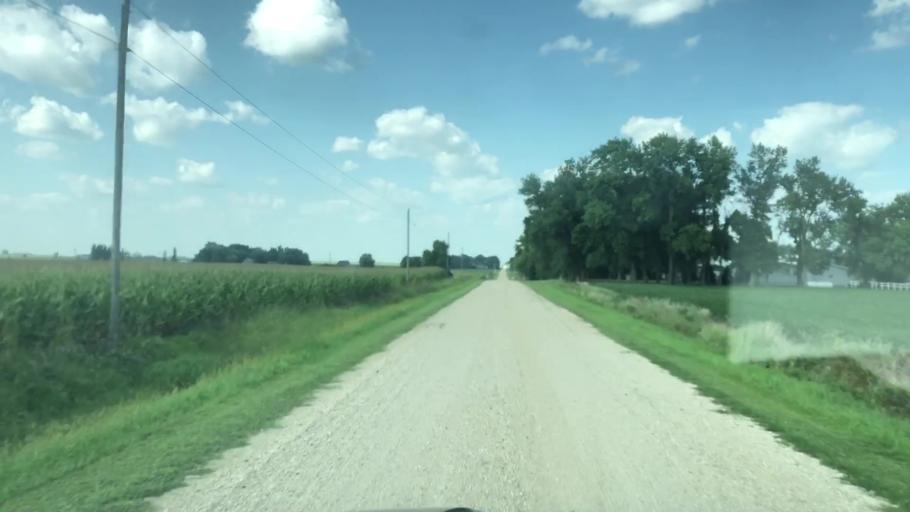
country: US
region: Iowa
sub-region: O'Brien County
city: Sheldon
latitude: 43.1652
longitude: -95.7822
